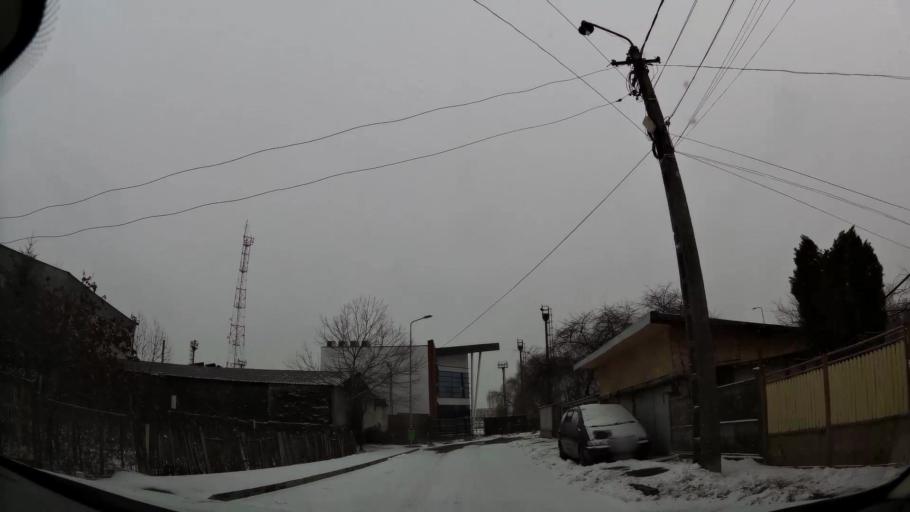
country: RO
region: Dambovita
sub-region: Municipiul Targoviste
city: Targoviste
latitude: 44.9158
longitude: 25.4637
